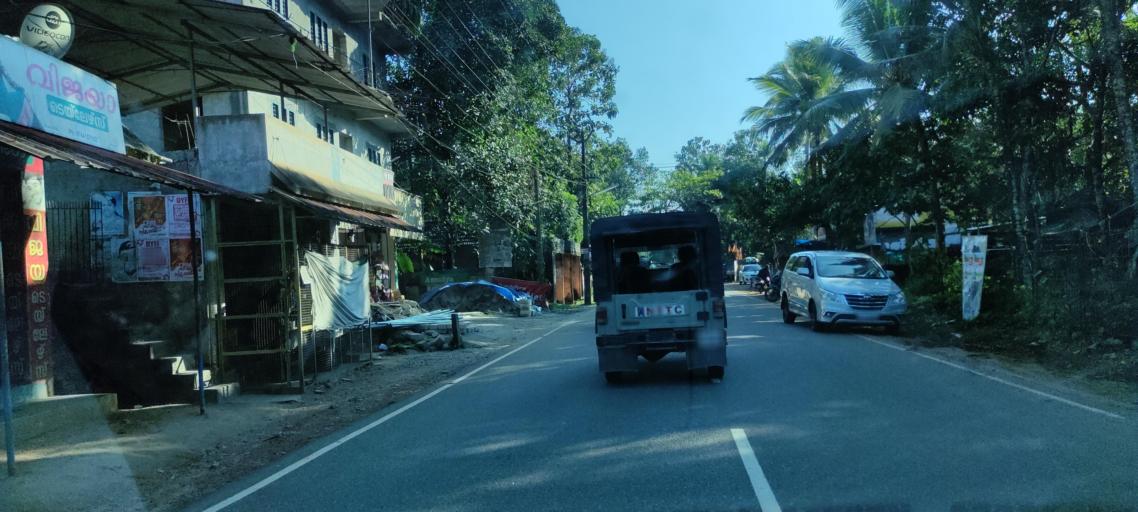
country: IN
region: Kerala
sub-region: Pattanamtitta
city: Adur
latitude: 9.1861
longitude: 76.7447
